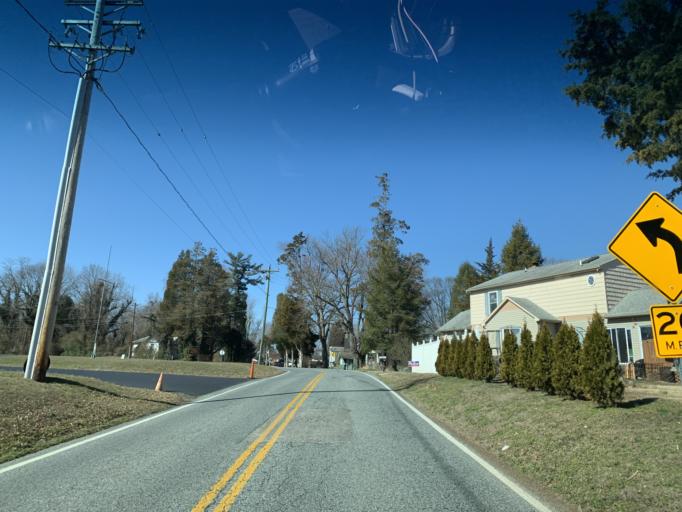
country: US
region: Maryland
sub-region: Cecil County
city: Charlestown
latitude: 39.4629
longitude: -75.8769
